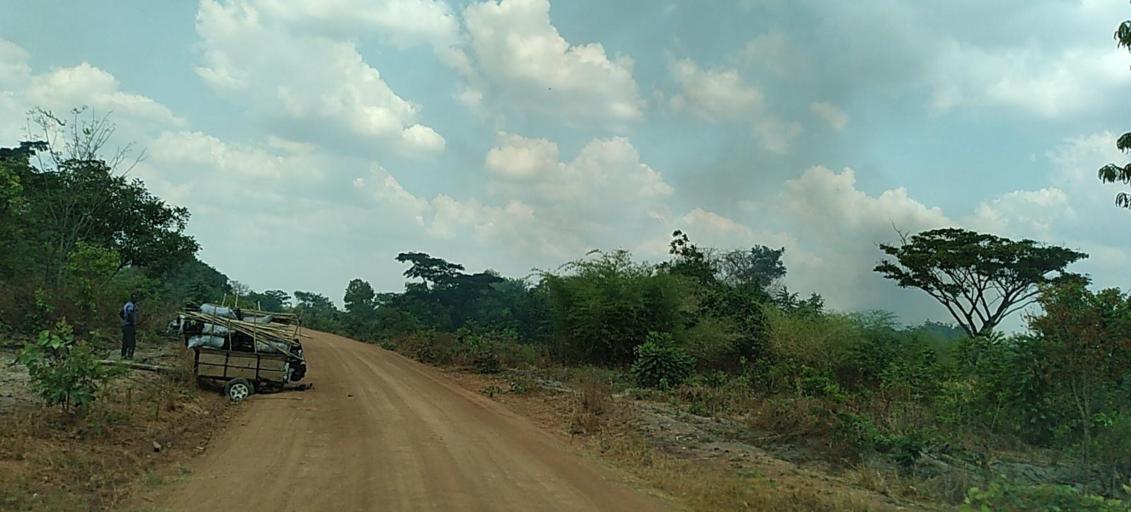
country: ZM
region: Copperbelt
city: Luanshya
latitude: -13.1405
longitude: 28.3343
